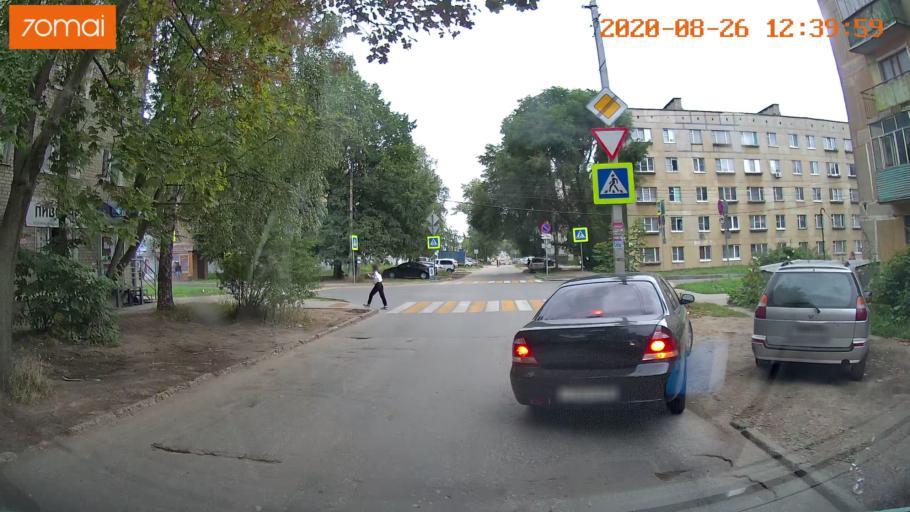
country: RU
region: Rjazan
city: Ryazan'
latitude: 54.6033
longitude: 39.7590
